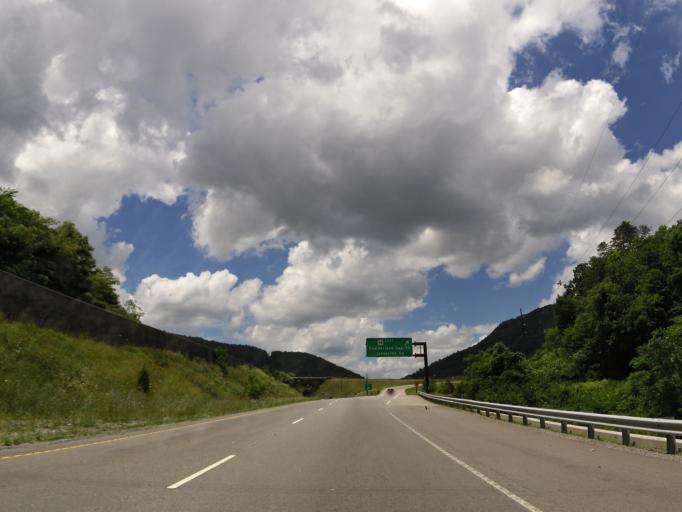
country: US
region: Tennessee
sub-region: Claiborne County
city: Harrogate
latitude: 36.5914
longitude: -83.6611
